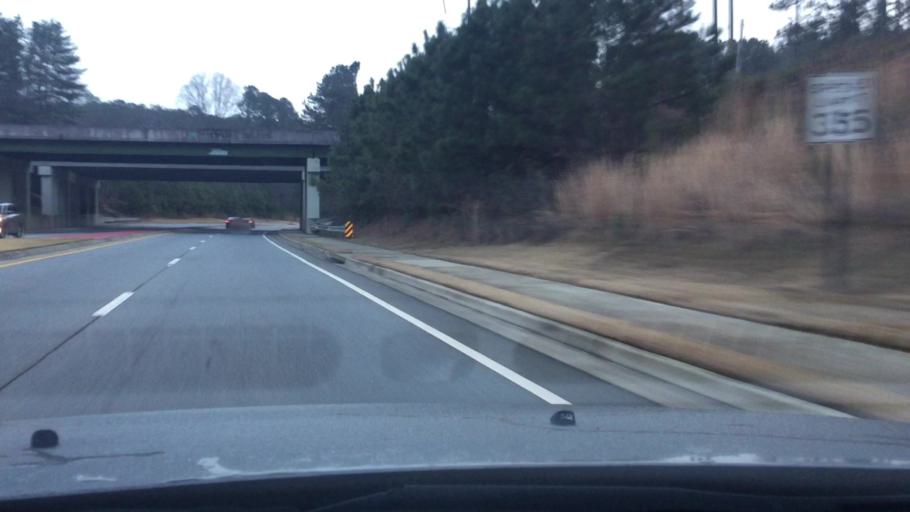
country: US
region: Georgia
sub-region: Cobb County
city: Kennesaw
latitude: 34.0289
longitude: -84.5616
